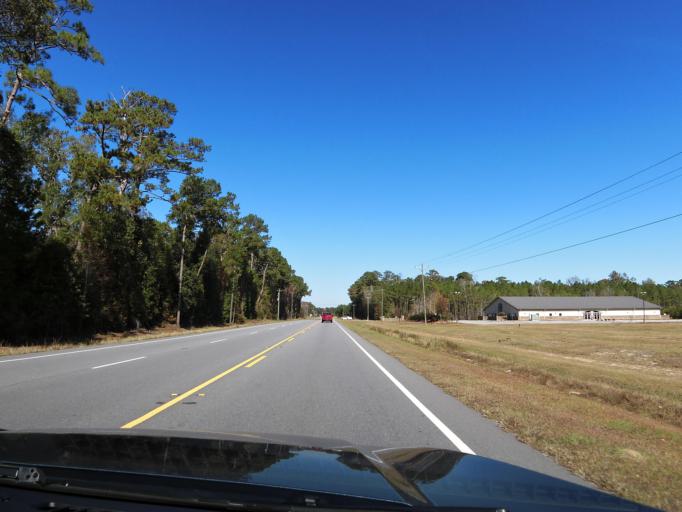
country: US
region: Georgia
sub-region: Liberty County
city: Midway
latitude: 31.8691
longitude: -81.3978
